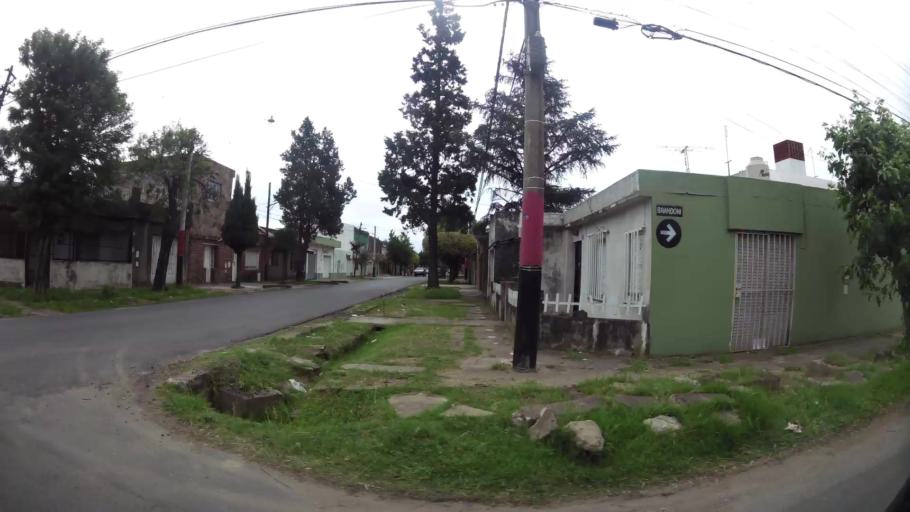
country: AR
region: Santa Fe
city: Gobernador Galvez
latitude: -33.0063
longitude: -60.6588
